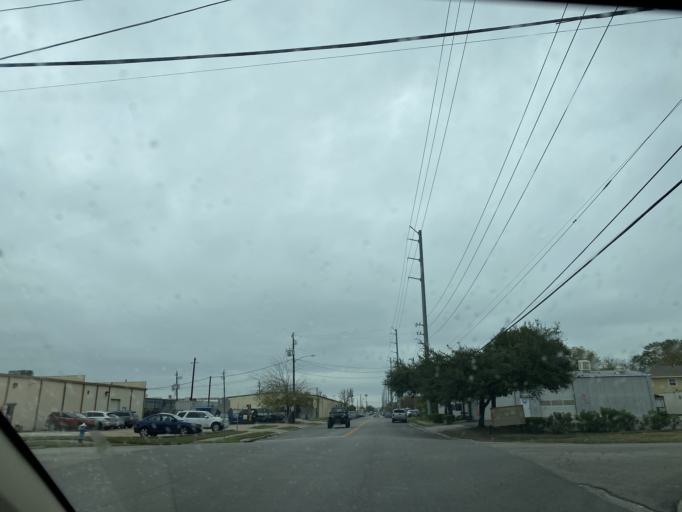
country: US
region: Texas
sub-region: Harris County
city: Piney Point Village
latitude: 29.7237
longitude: -95.5194
